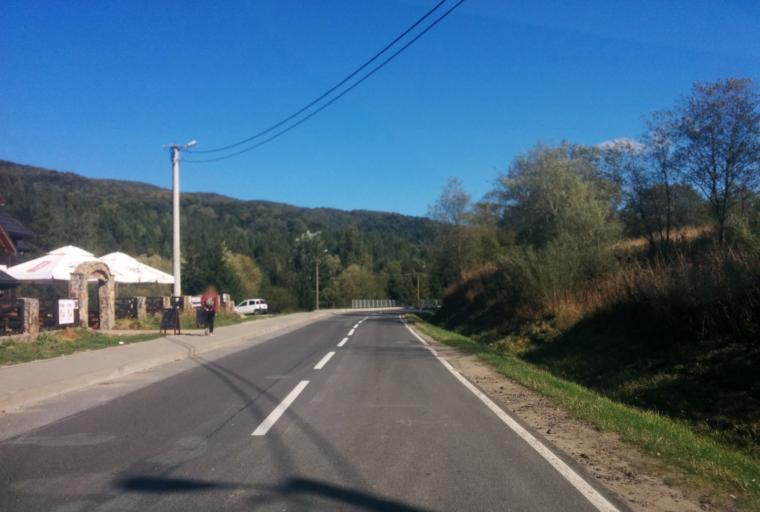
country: PL
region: Subcarpathian Voivodeship
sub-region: Powiat bieszczadzki
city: Lutowiska
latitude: 49.1063
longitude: 22.6500
